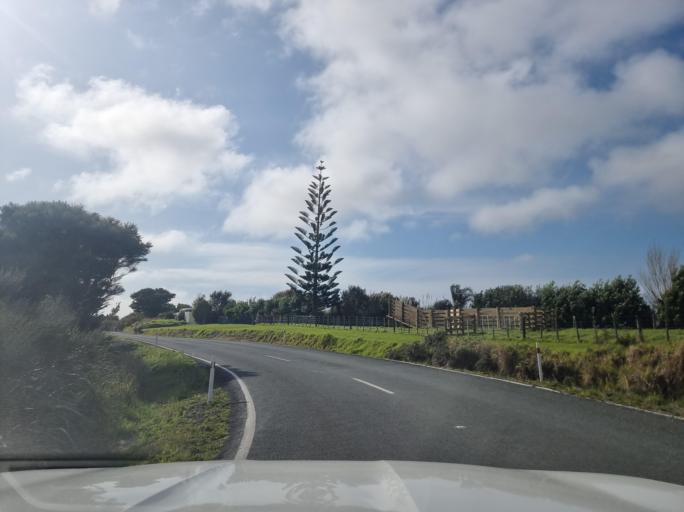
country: NZ
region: Northland
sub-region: Whangarei
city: Ruakaka
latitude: -36.0135
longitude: 174.4635
